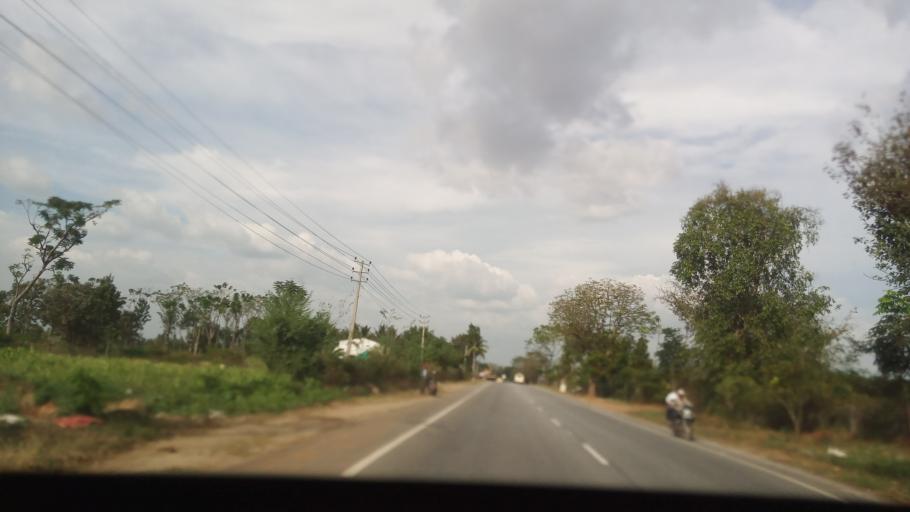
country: IN
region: Karnataka
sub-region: Mandya
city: Maddur
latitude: 12.6749
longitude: 77.0570
